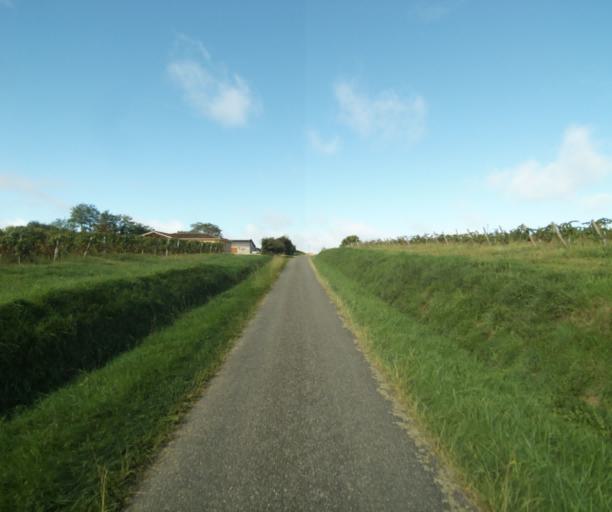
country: FR
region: Midi-Pyrenees
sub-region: Departement du Gers
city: Cazaubon
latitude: 43.8508
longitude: -0.0485
